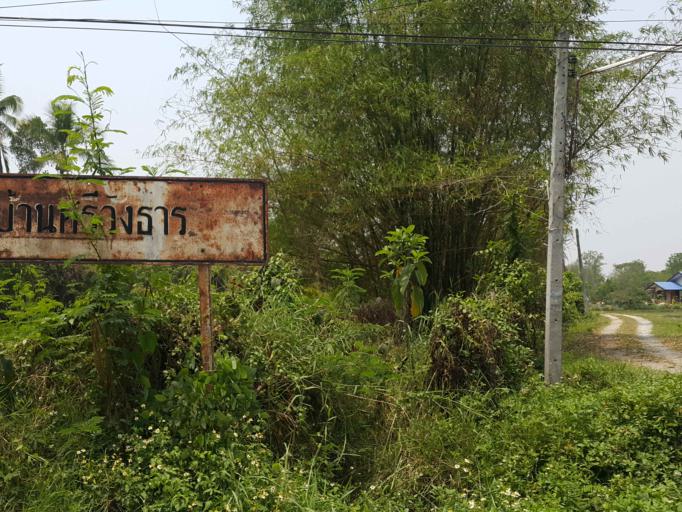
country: TH
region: Chiang Mai
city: San Sai
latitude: 18.8958
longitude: 99.0729
